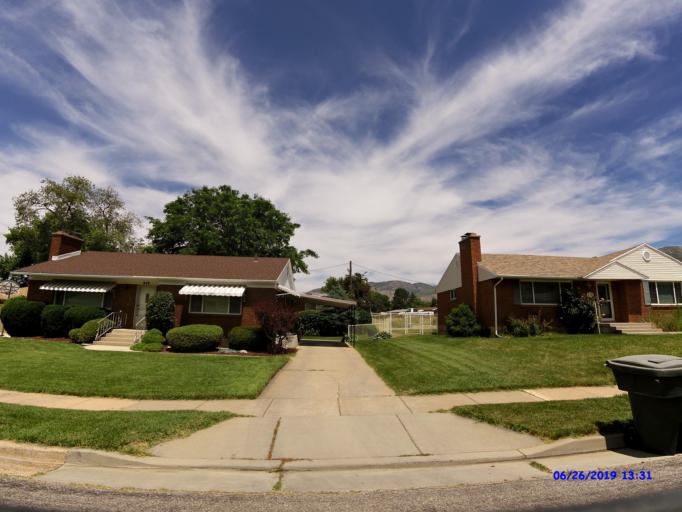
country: US
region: Utah
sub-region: Weber County
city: South Ogden
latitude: 41.2010
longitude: -111.9586
